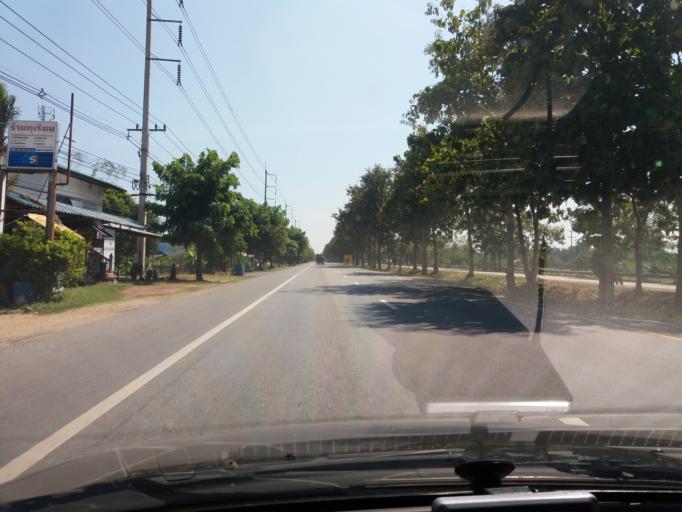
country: TH
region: Chai Nat
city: Sankhaburi
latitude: 15.0932
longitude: 100.1384
